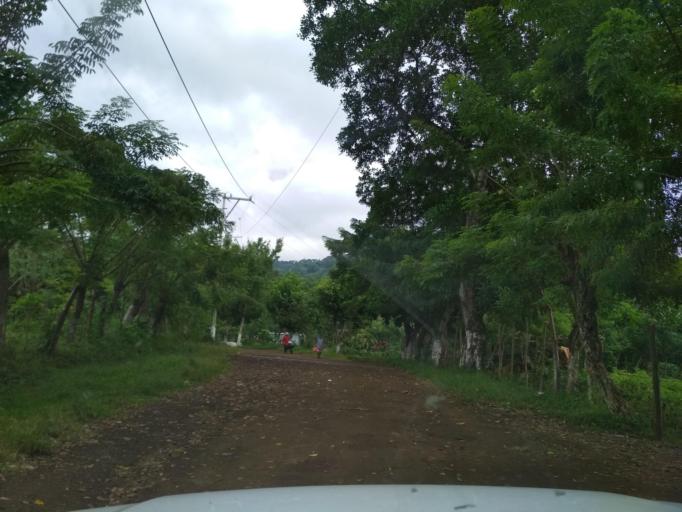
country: MX
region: Veracruz
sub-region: San Andres Tuxtla
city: Matacapan
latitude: 18.4442
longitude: -95.1777
